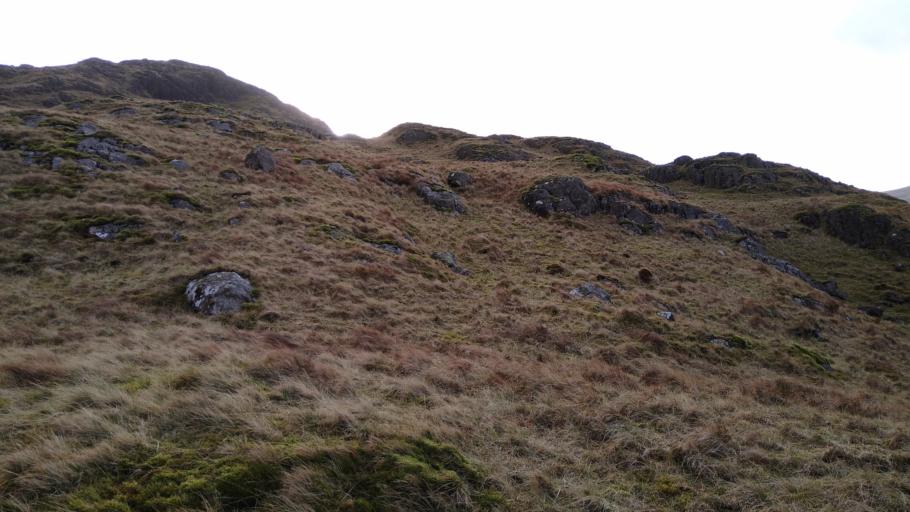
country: GB
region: England
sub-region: Cumbria
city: Keswick
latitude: 54.4088
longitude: -3.1981
